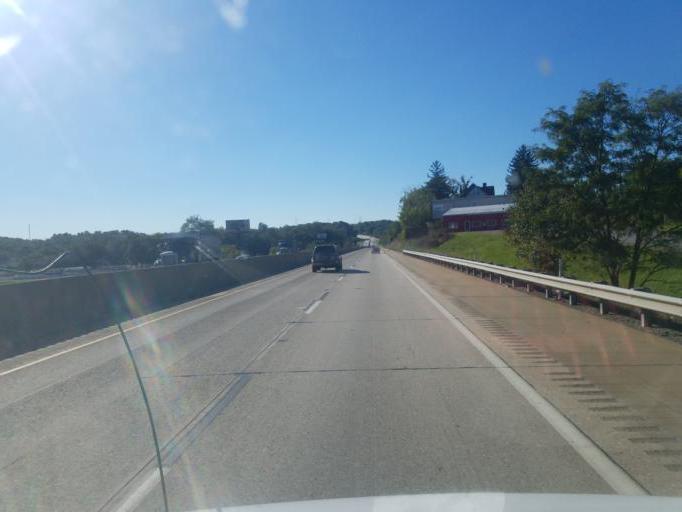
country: US
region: Pennsylvania
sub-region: Allegheny County
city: Enlow
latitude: 40.4397
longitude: -80.2278
